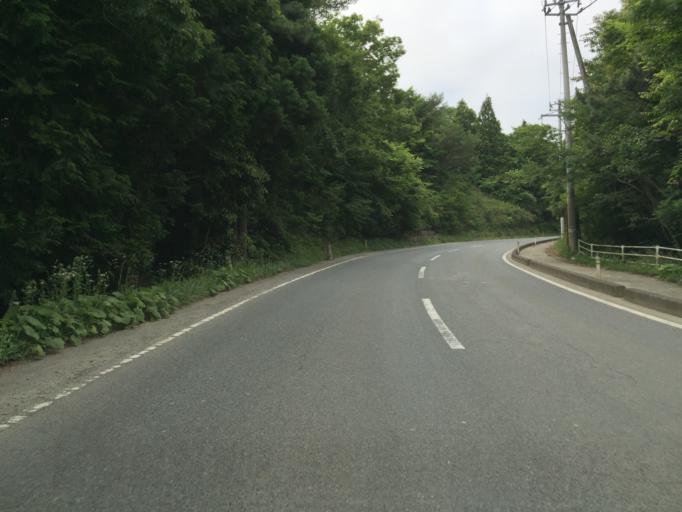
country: JP
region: Fukushima
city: Namie
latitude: 37.7093
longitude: 141.0070
